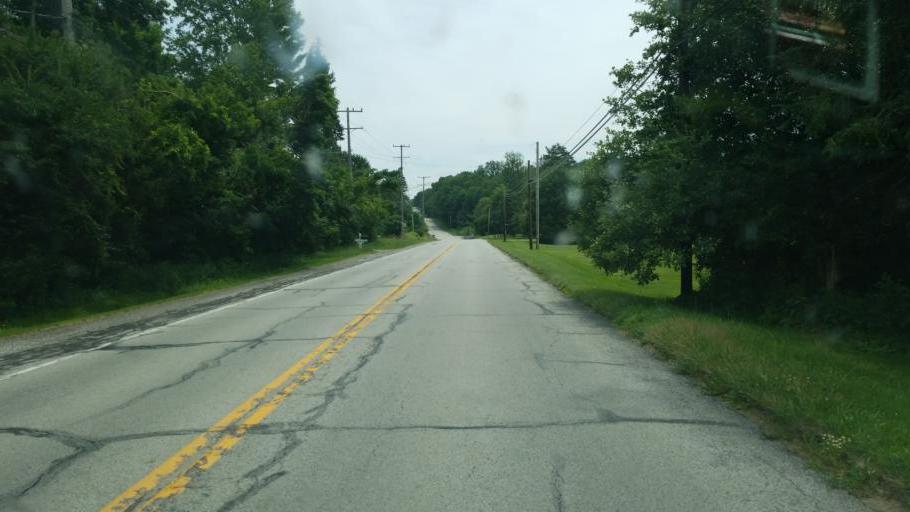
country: US
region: Ohio
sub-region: Geauga County
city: Bainbridge
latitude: 41.3875
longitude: -81.2603
